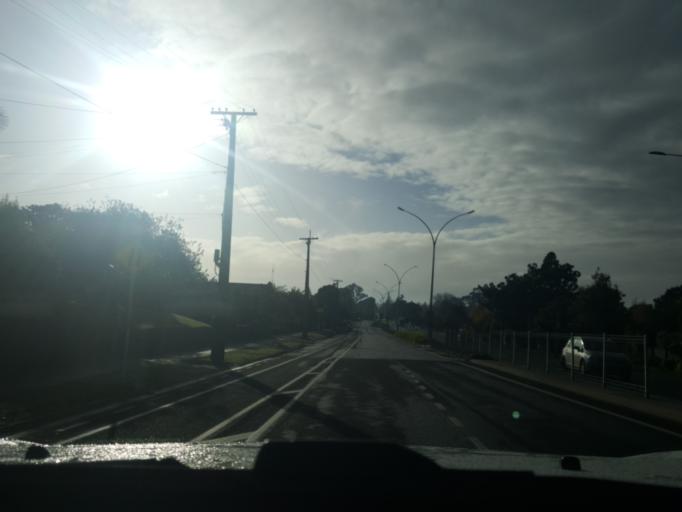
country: NZ
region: Waikato
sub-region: Hamilton City
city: Hamilton
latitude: -37.8008
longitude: 175.3227
